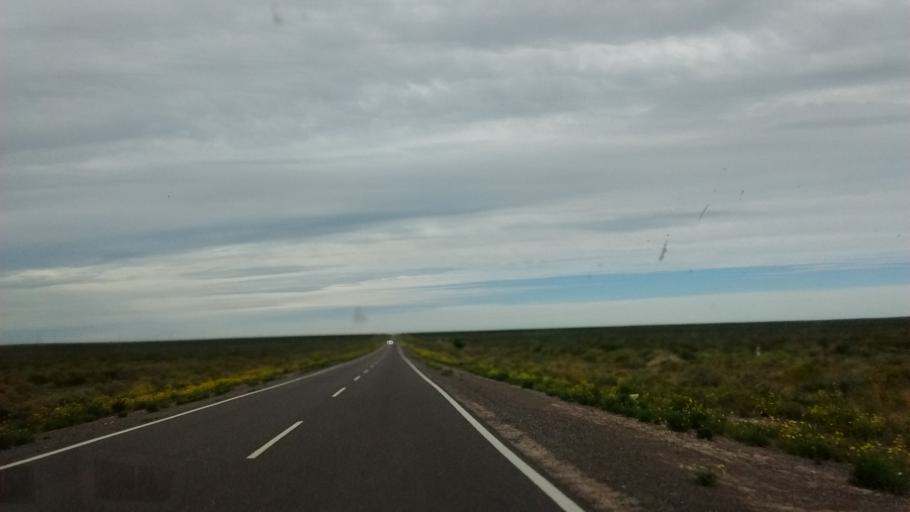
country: AR
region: Rio Negro
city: Catriel
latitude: -38.2385
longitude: -67.9842
